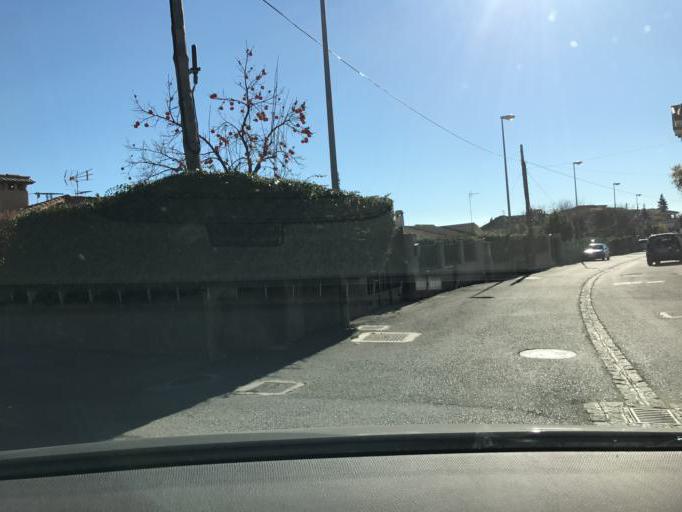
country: ES
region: Andalusia
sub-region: Provincia de Granada
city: Viznar
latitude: 37.2125
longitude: -3.5560
